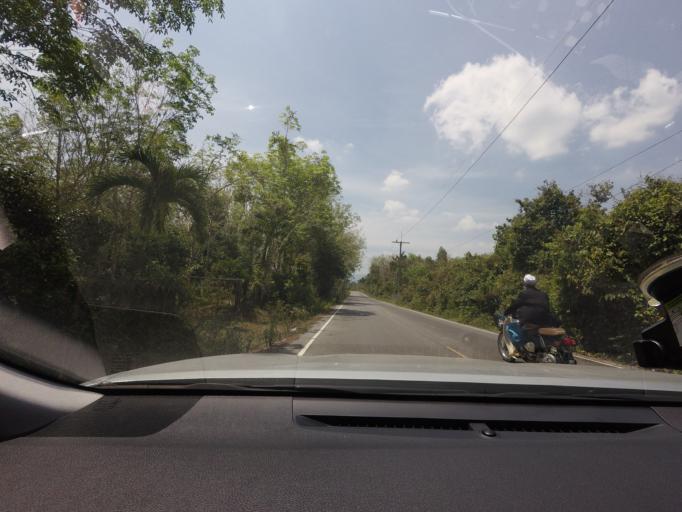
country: TH
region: Narathiwat
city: Rueso
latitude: 6.3837
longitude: 101.5066
